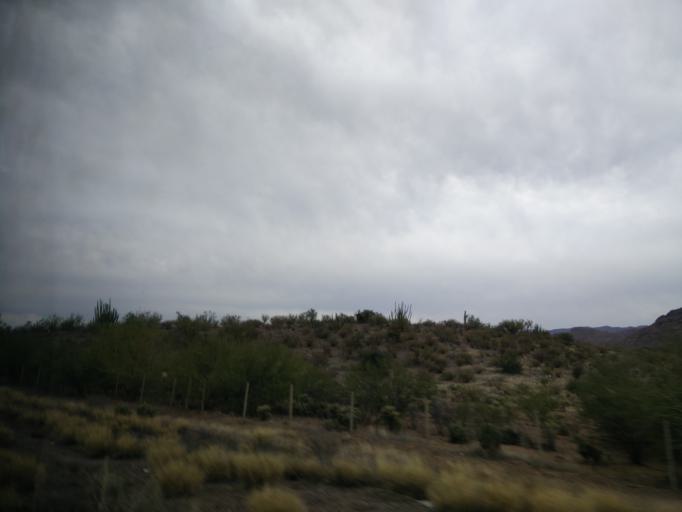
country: MX
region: Sonora
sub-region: Hermosillo
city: Miguel Aleman (La Doce)
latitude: 28.4970
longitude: -111.0430
